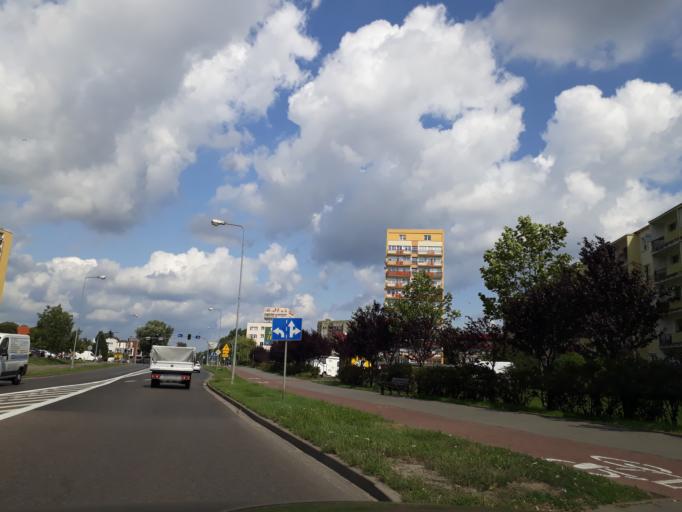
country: PL
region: West Pomeranian Voivodeship
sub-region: Swinoujscie
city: Swinoujscie
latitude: 53.9035
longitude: 14.2362
